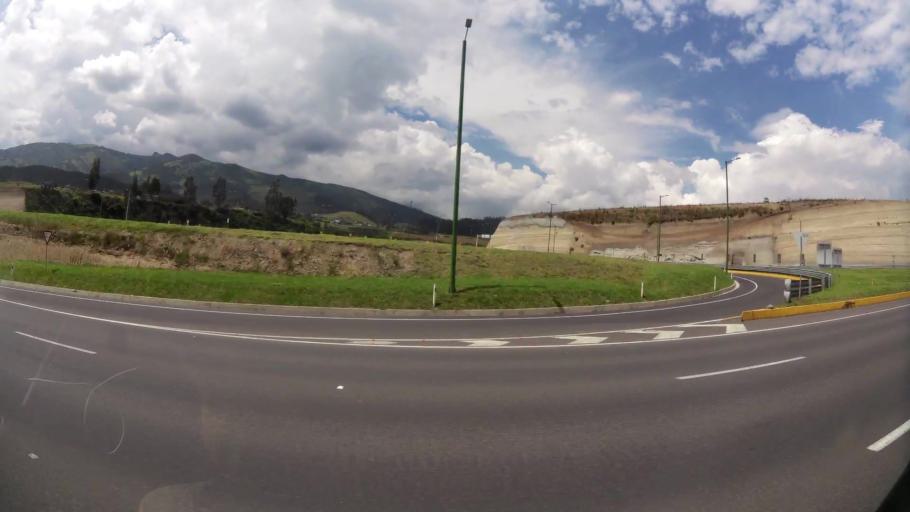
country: EC
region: Pichincha
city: Sangolqui
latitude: -0.2146
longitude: -78.3346
